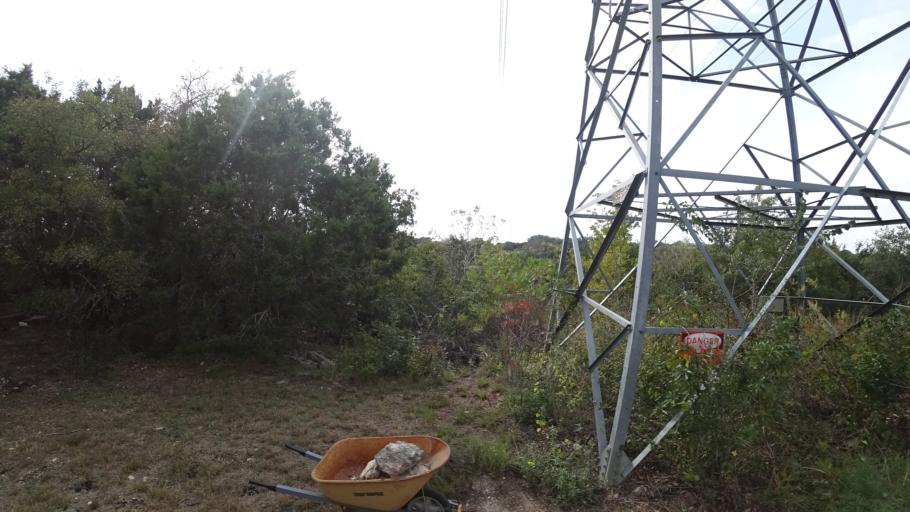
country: US
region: Texas
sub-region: Travis County
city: Hudson Bend
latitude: 30.3876
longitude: -97.9230
